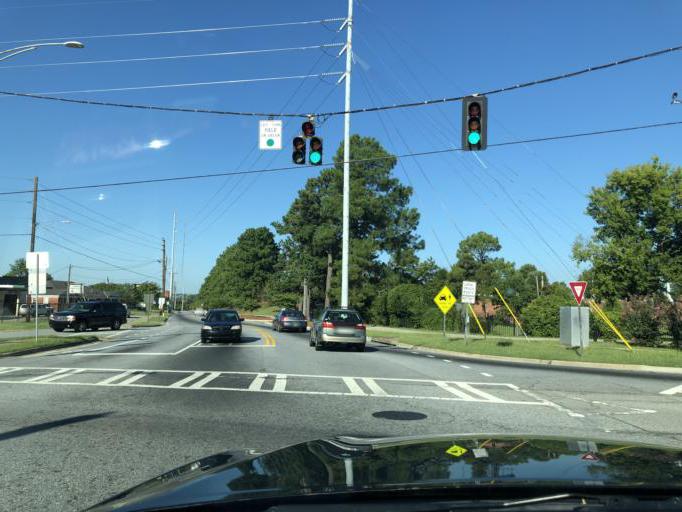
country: US
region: Georgia
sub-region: Muscogee County
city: Columbus
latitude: 32.4775
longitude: -84.9796
